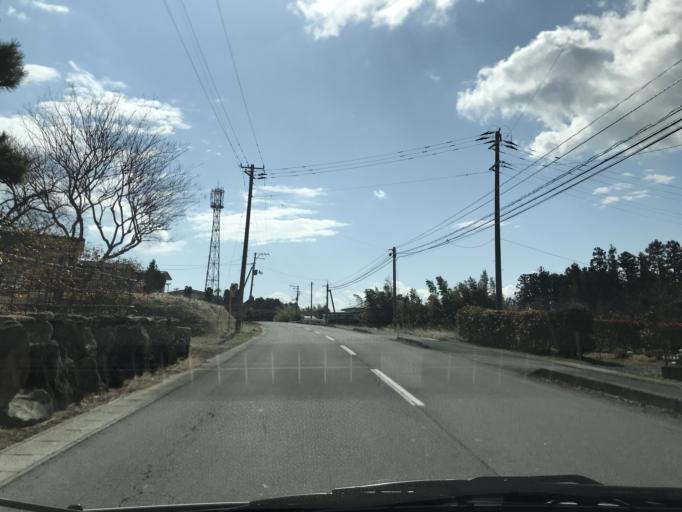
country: JP
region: Miyagi
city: Wakuya
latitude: 38.6953
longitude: 141.1640
